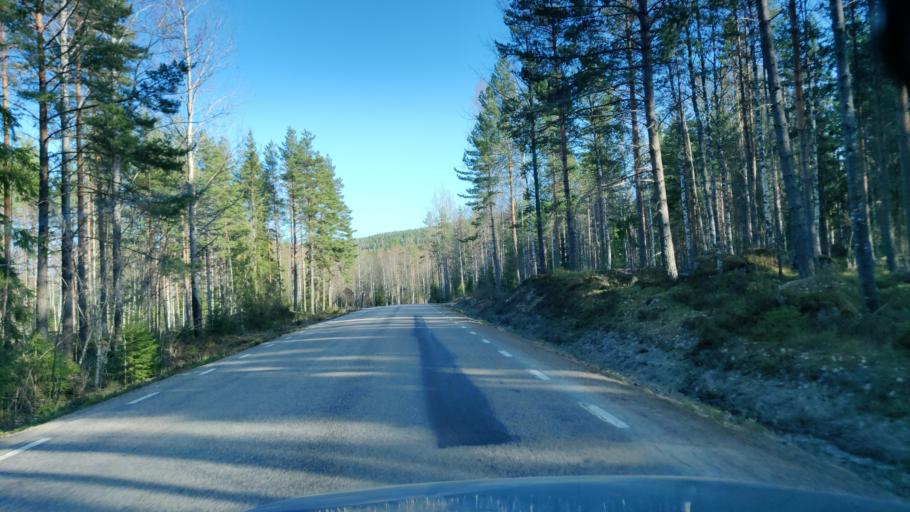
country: SE
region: Vaermland
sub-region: Hagfors Kommun
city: Ekshaerad
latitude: 59.9836
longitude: 13.3555
